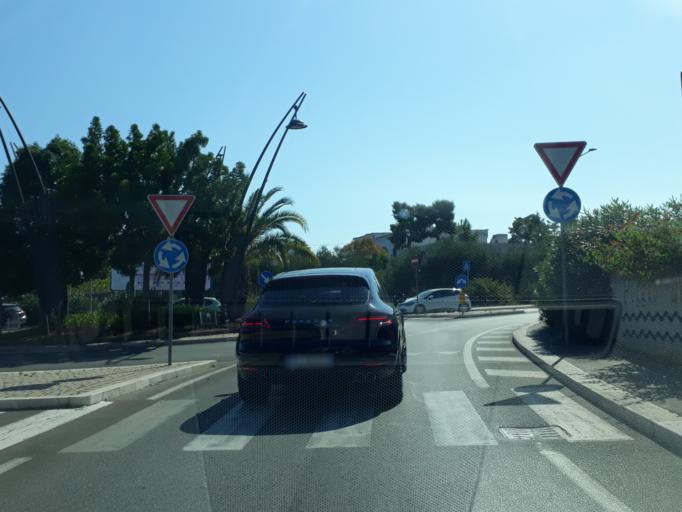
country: IT
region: Apulia
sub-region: Provincia di Bari
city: Monopoli
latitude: 40.9464
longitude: 17.2938
